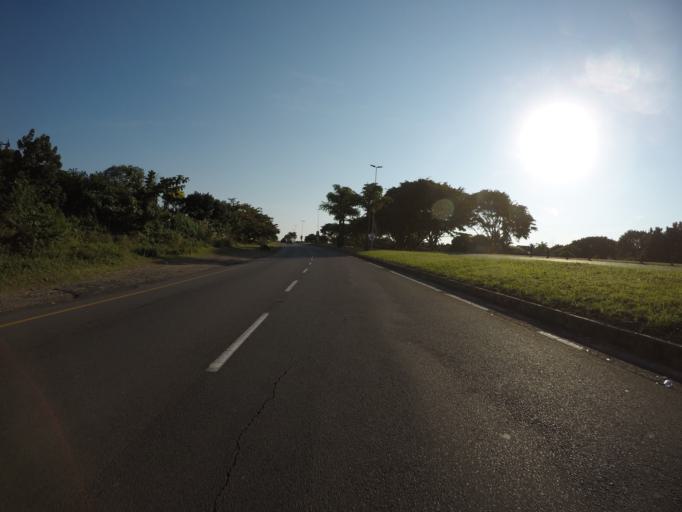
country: ZA
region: KwaZulu-Natal
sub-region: uThungulu District Municipality
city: Richards Bay
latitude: -28.7674
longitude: 32.0600
